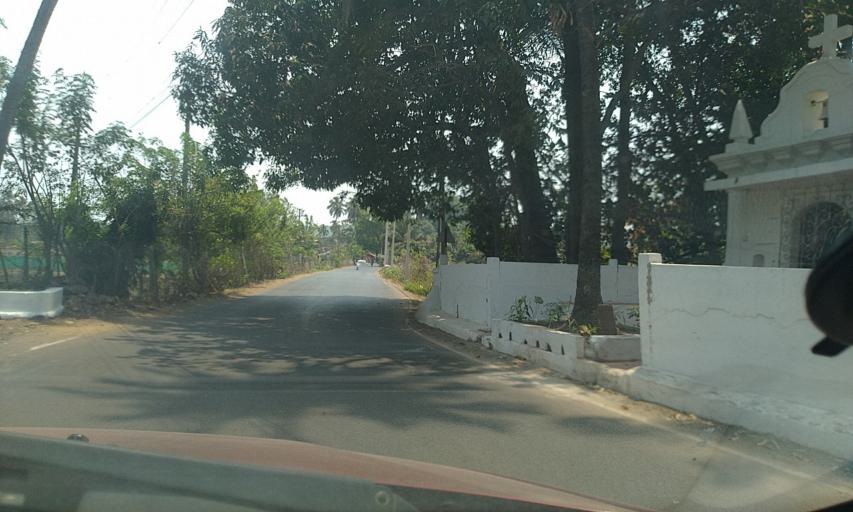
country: IN
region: Goa
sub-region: North Goa
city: Vagator
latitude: 15.5928
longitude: 73.7604
